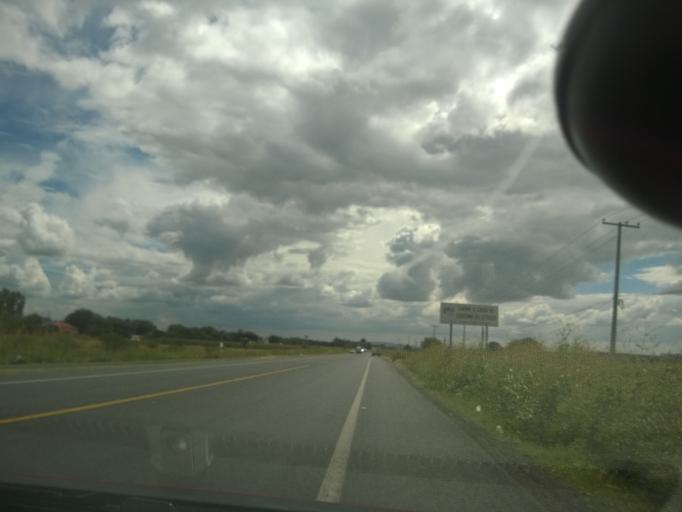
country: MX
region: Guanajuato
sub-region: Leon
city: El CERESO
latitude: 21.0162
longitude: -101.6994
